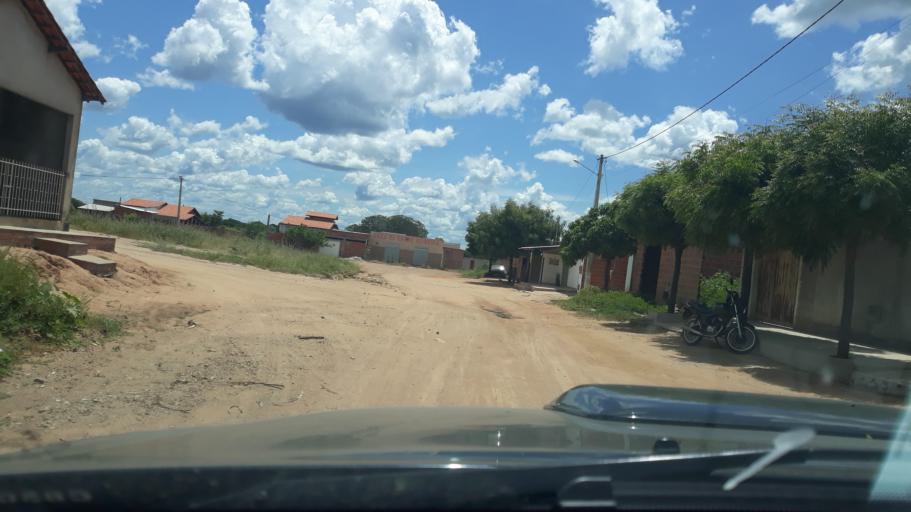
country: BR
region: Bahia
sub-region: Riacho De Santana
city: Riacho de Santana
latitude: -13.9102
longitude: -42.8496
